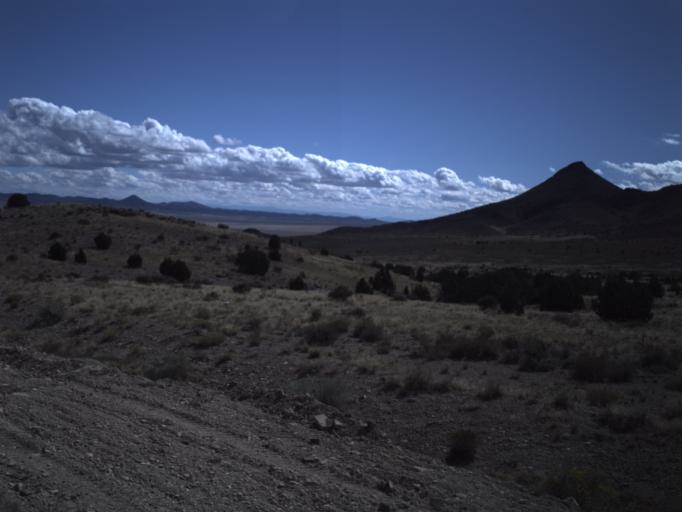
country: US
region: Utah
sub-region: Beaver County
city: Milford
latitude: 38.5036
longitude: -113.5085
